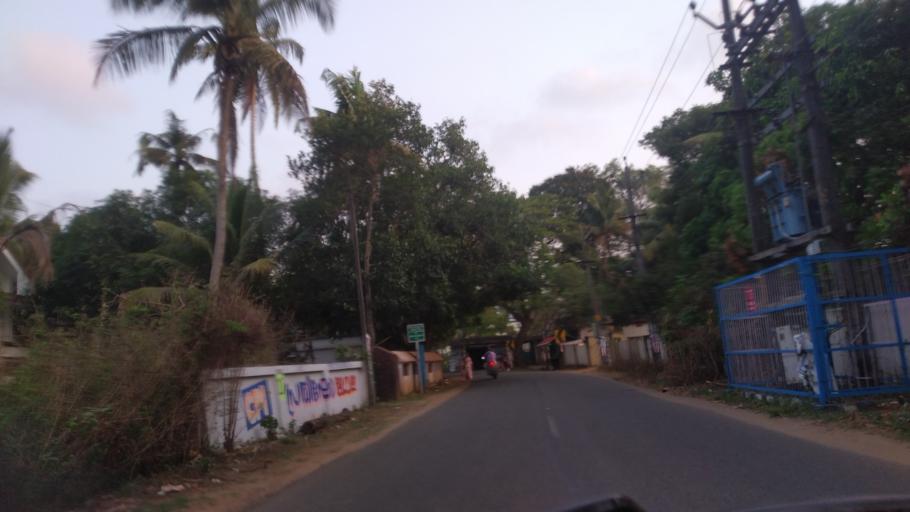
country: IN
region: Kerala
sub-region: Thrissur District
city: Kodungallur
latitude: 10.2289
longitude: 76.1551
